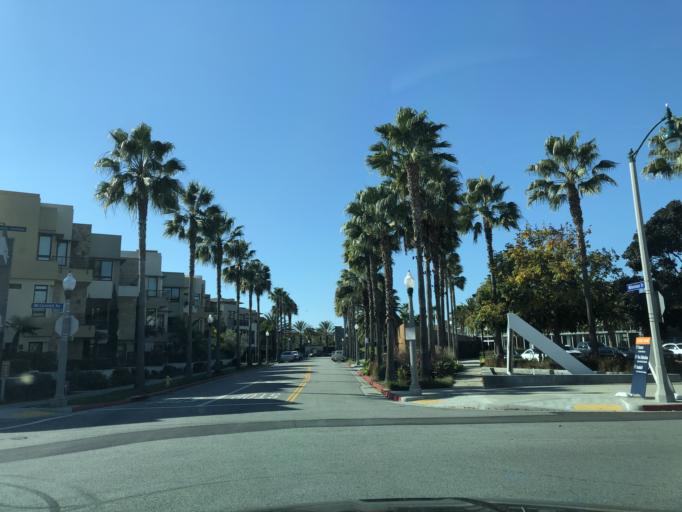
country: US
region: California
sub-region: Los Angeles County
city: Marina del Rey
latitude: 33.9754
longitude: -118.4177
